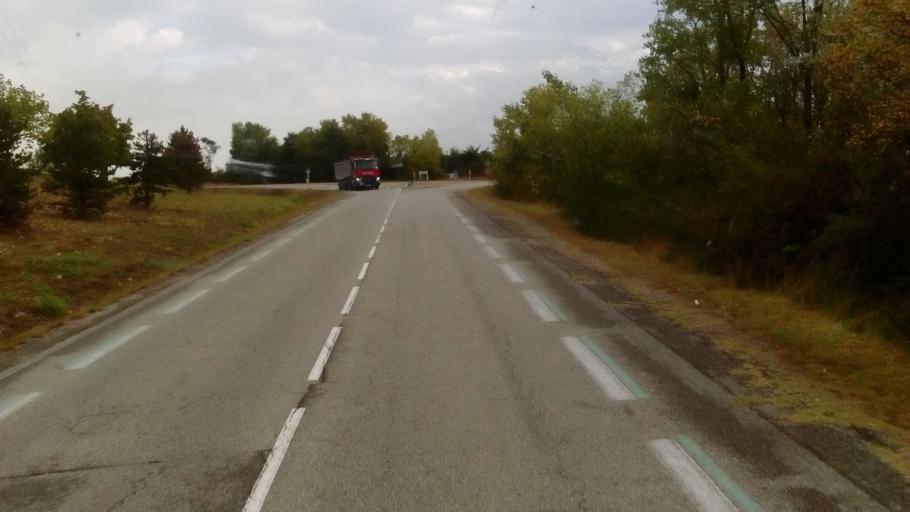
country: FR
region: Rhone-Alpes
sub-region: Departement de l'Ardeche
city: Cornas
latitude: 44.9690
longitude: 4.8751
